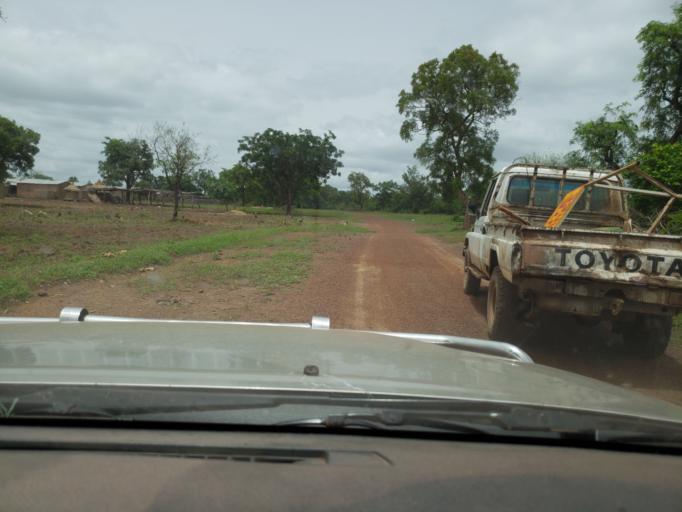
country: ML
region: Koulikoro
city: Kangaba
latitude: 12.0672
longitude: -8.4963
